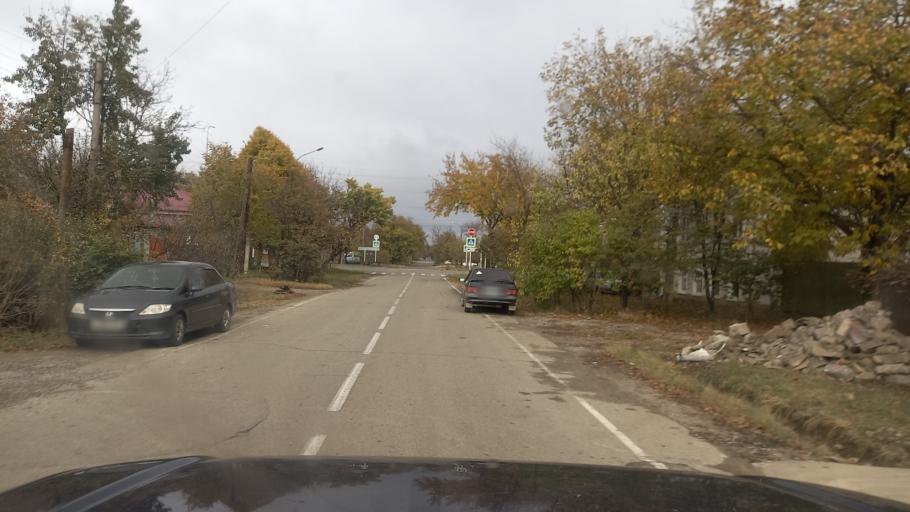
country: RU
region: Adygeya
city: Maykop
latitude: 44.6073
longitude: 40.1164
